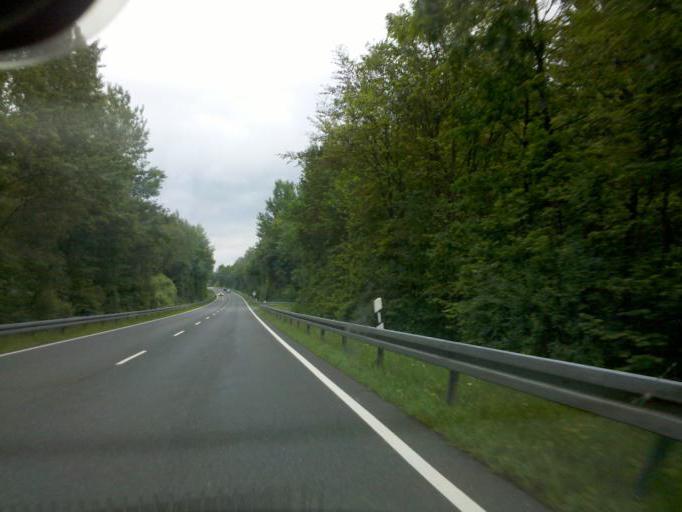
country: DE
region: North Rhine-Westphalia
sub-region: Regierungsbezirk Arnsberg
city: Wilnsdorf
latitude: 50.7746
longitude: 8.1483
